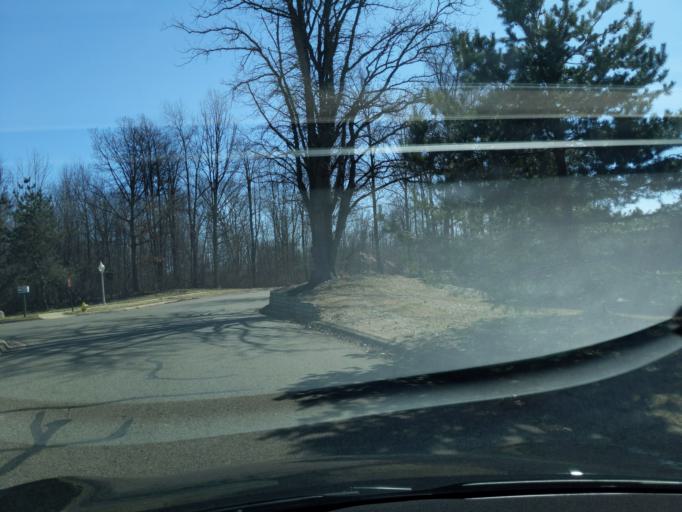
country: US
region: Michigan
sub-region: Eaton County
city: Waverly
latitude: 42.7294
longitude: -84.6671
